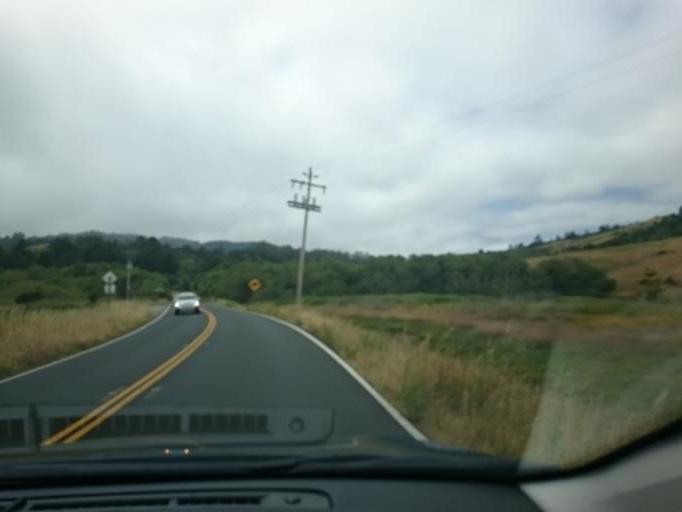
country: US
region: California
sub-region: Marin County
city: Bolinas
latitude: 37.9341
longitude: -122.6955
